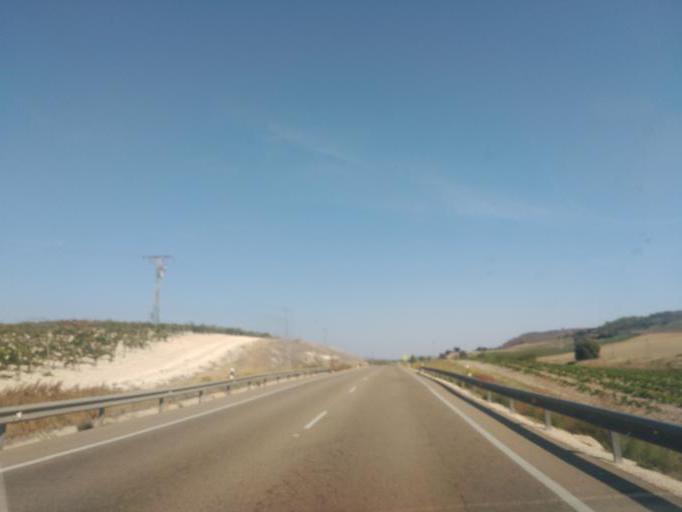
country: ES
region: Castille and Leon
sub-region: Provincia de Valladolid
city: Valbuena de Duero
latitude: 41.6238
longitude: -4.2636
